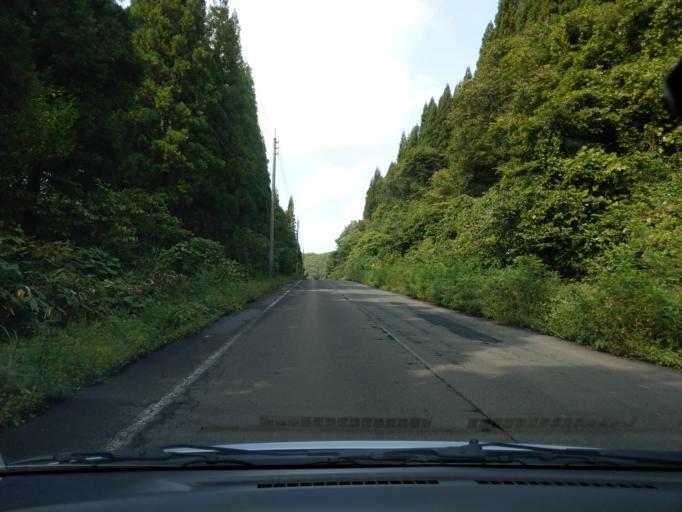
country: JP
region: Akita
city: Omagari
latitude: 39.4432
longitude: 140.3300
